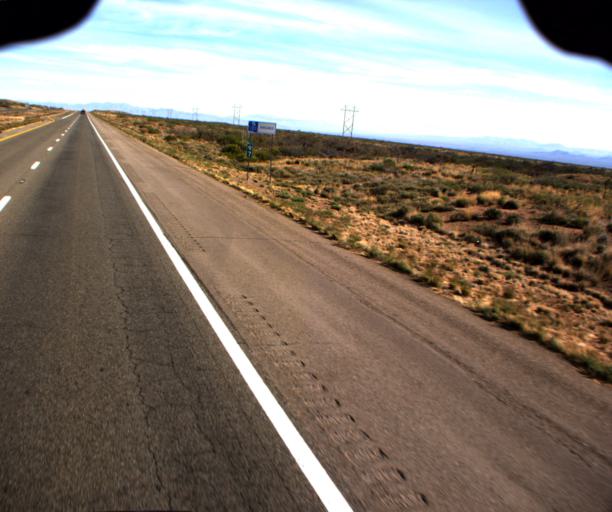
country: US
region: Arizona
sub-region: Graham County
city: Swift Trail Junction
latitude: 32.4919
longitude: -109.6733
